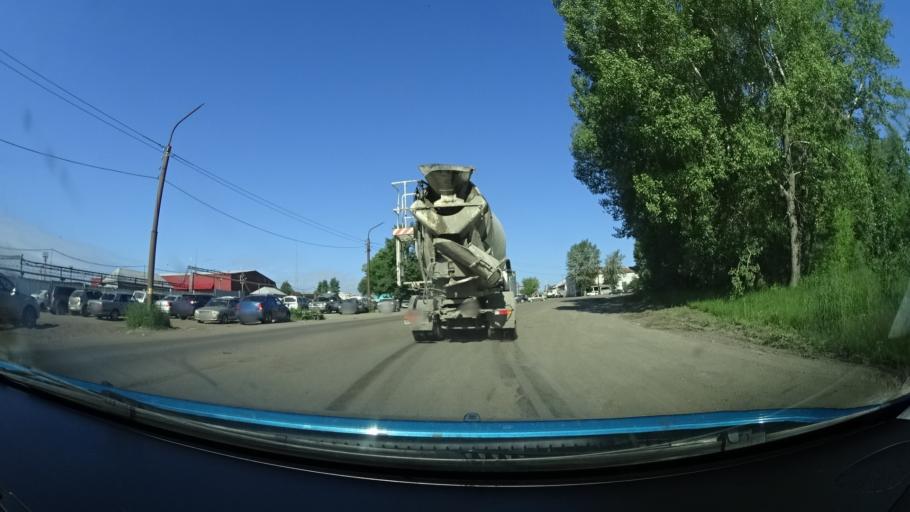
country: RU
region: Bashkortostan
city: Ufa
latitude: 54.8556
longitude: 56.0977
